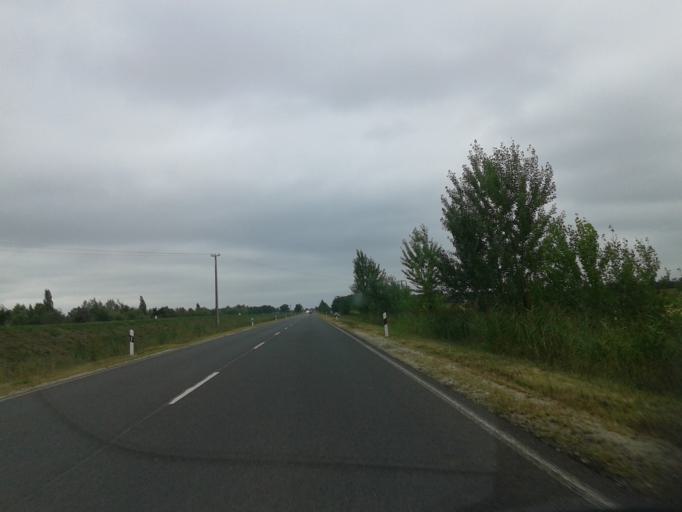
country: HU
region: Bacs-Kiskun
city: Solt
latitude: 46.7742
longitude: 19.0068
